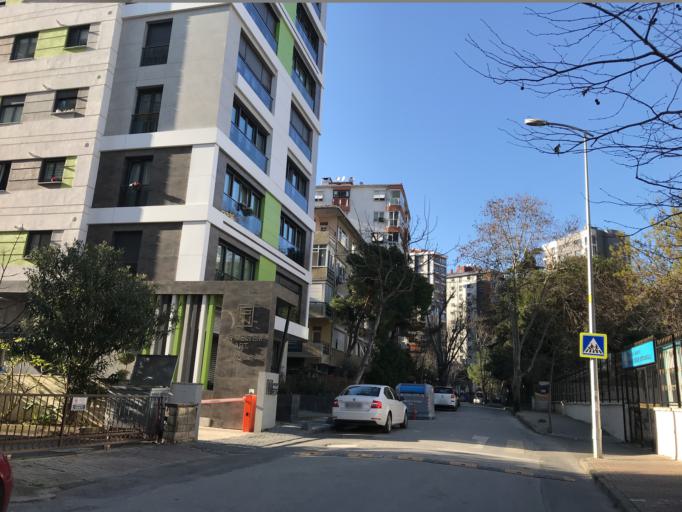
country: TR
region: Istanbul
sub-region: Atasehir
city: Atasehir
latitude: 40.9635
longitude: 29.0951
